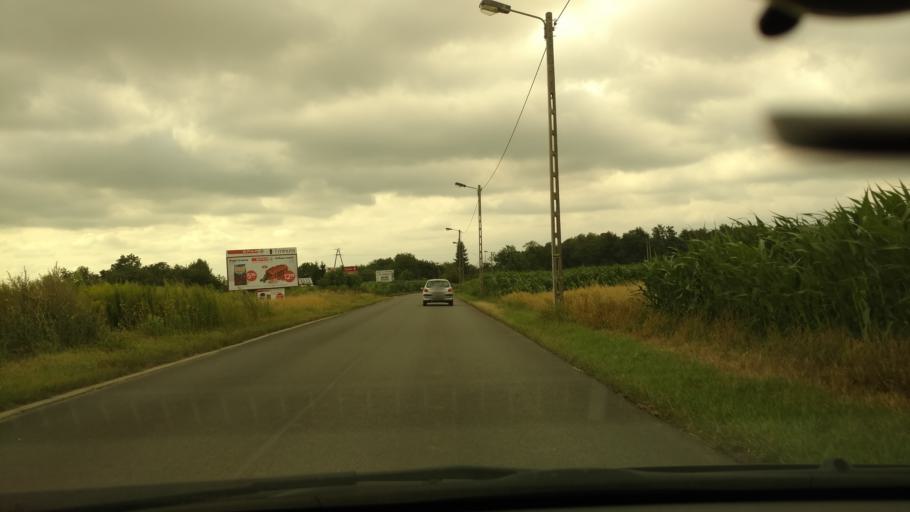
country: PL
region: Lesser Poland Voivodeship
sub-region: Powiat krakowski
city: Zielonki
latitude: 50.1140
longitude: 19.9428
